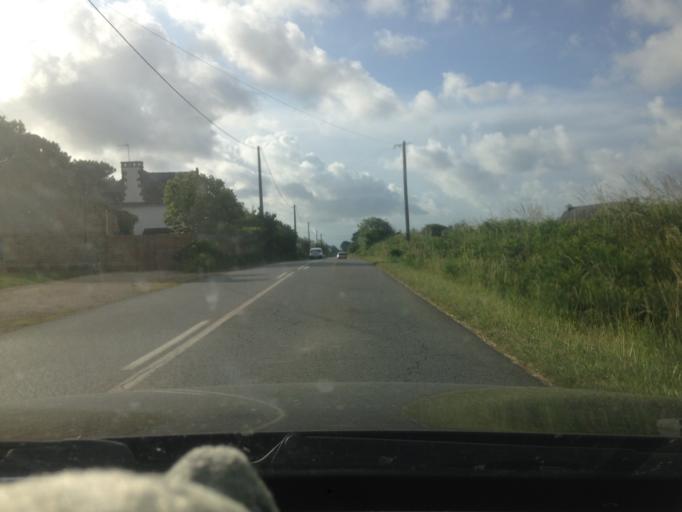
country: FR
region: Brittany
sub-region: Departement du Morbihan
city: Plouharnel
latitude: 47.5946
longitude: -3.1040
